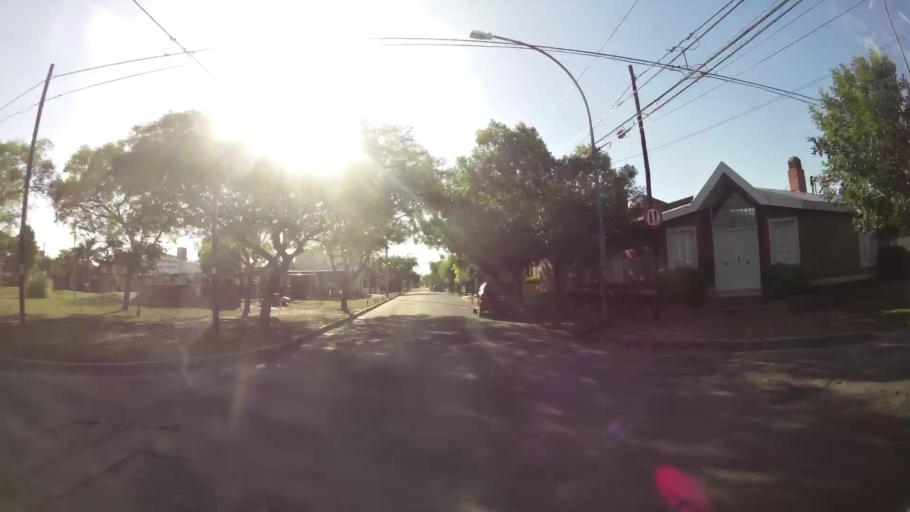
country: AR
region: Cordoba
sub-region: Departamento de Capital
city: Cordoba
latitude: -31.3580
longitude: -64.2130
